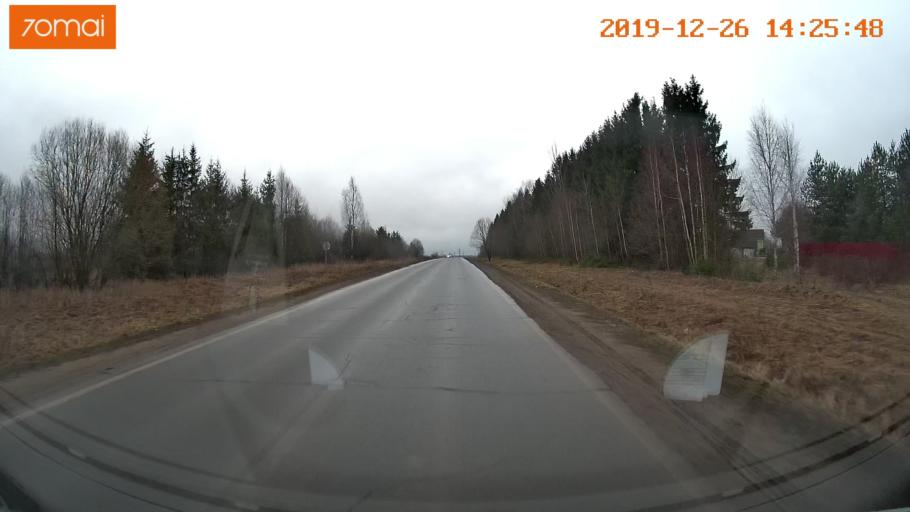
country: RU
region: Jaroslavl
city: Poshekhon'ye
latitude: 58.4916
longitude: 39.0906
